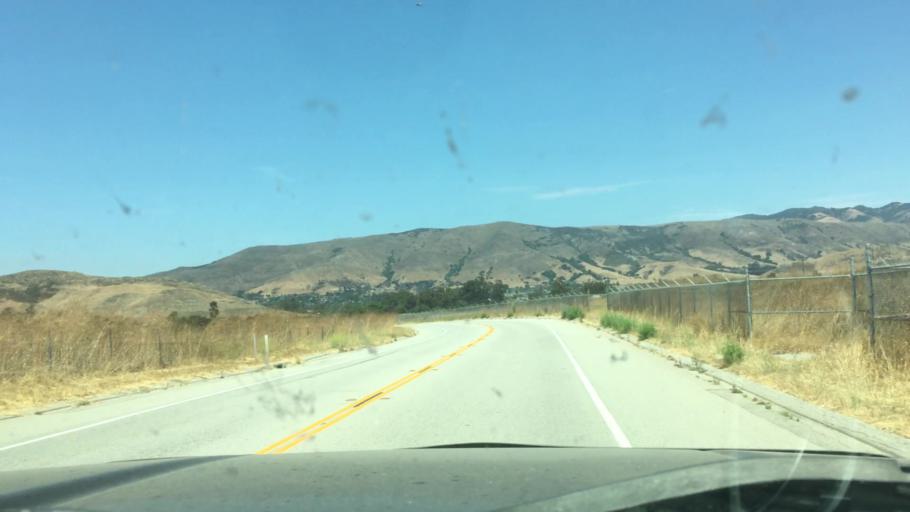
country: US
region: California
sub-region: San Luis Obispo County
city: San Luis Obispo
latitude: 35.2402
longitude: -120.6540
